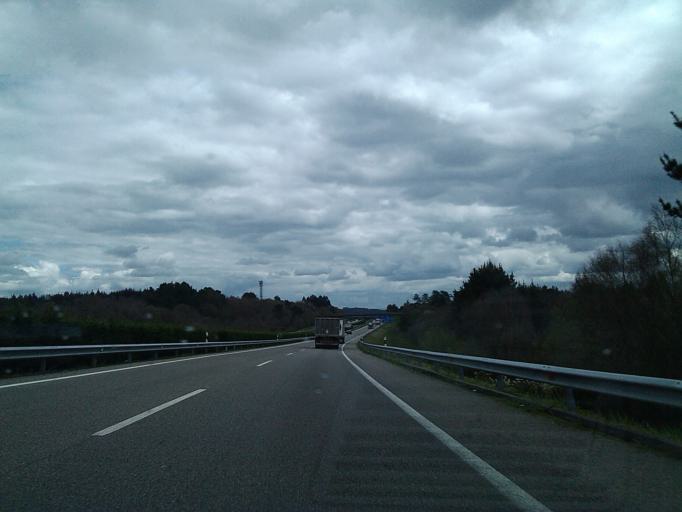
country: ES
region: Galicia
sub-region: Provincia de Lugo
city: Guitiriz
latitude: 43.1881
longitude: -7.8494
